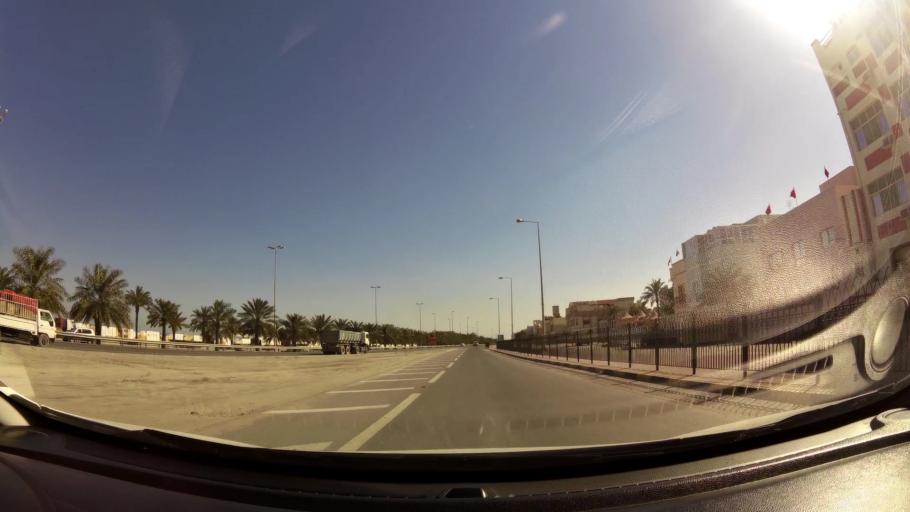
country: BH
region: Muharraq
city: Al Hadd
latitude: 26.2394
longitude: 50.6578
